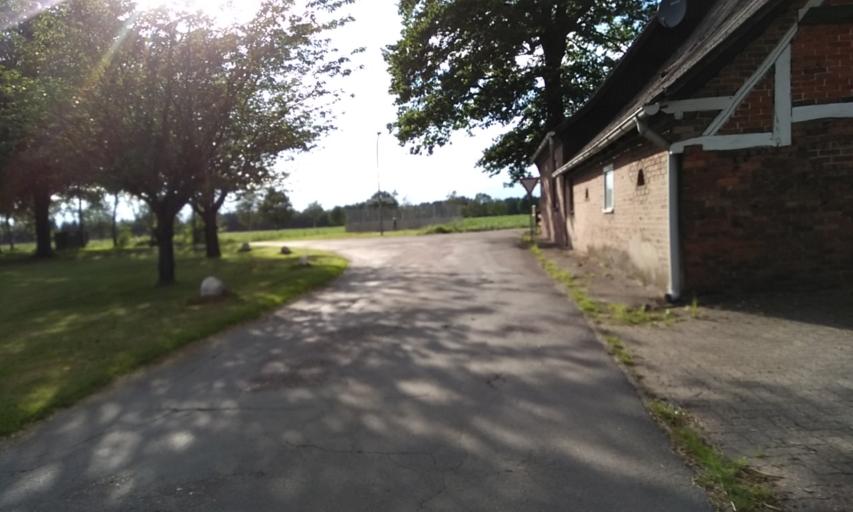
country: DE
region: Lower Saxony
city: Vierden
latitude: 53.3580
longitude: 9.4679
